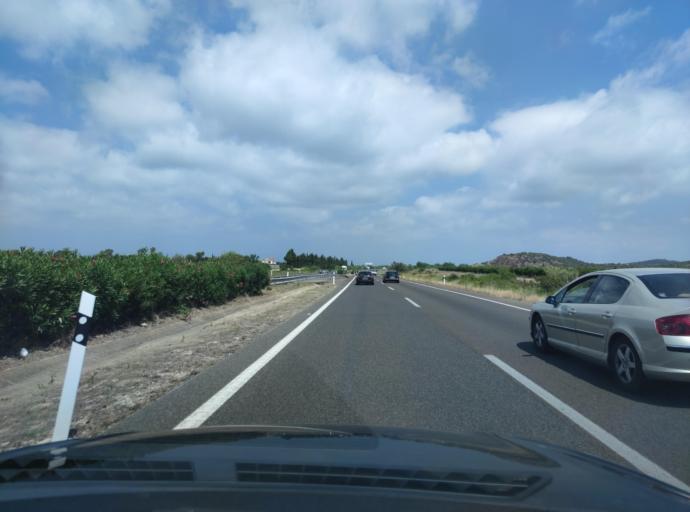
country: ES
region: Valencia
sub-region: Provincia de Castello
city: Vinaros
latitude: 40.4819
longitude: 0.4179
